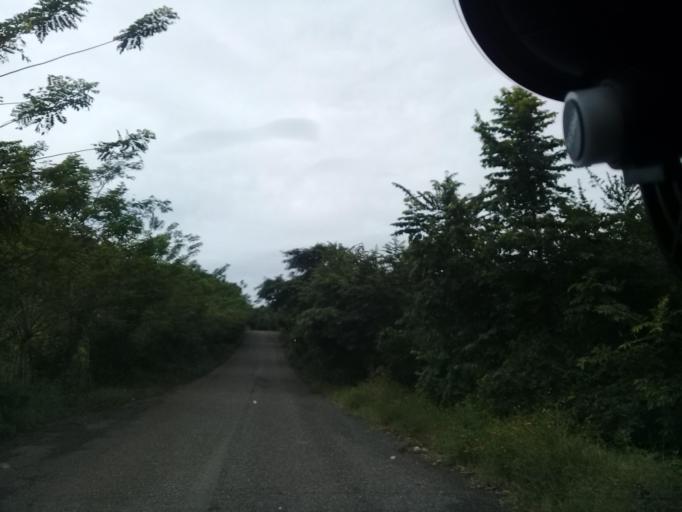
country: MX
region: Hidalgo
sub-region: Huejutla de Reyes
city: Chalahuiyapa
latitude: 21.2103
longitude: -98.3589
